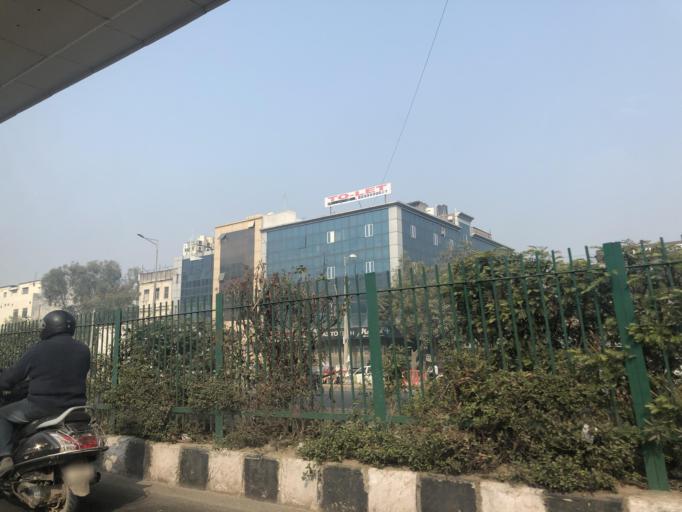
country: IN
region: NCT
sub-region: West Delhi
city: Nangloi Jat
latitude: 28.6808
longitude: 77.0826
